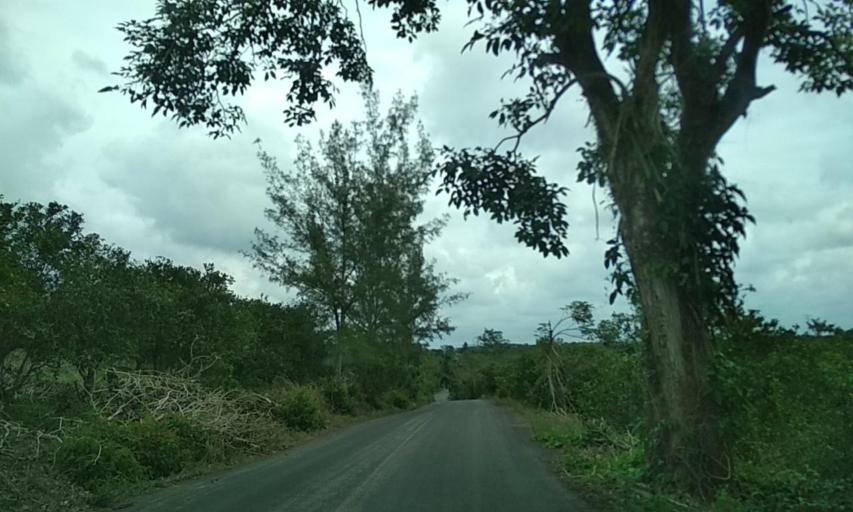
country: MX
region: Veracruz
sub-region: Papantla
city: El Chote
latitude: 20.3459
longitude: -97.3880
